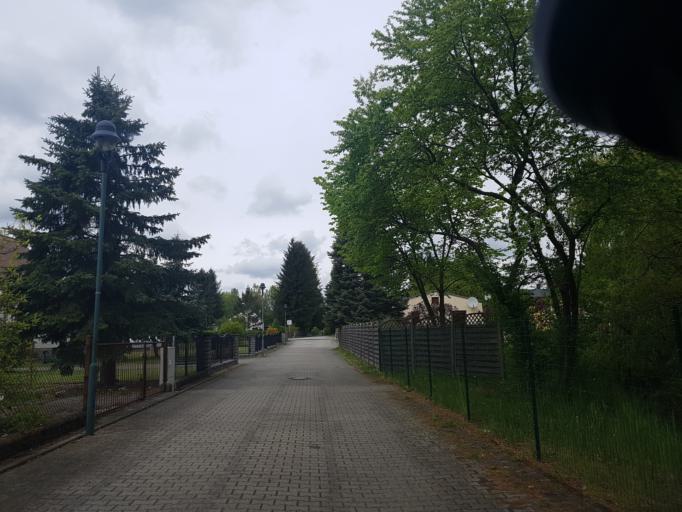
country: DE
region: Brandenburg
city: Tschernitz
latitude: 51.6214
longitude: 14.5961
